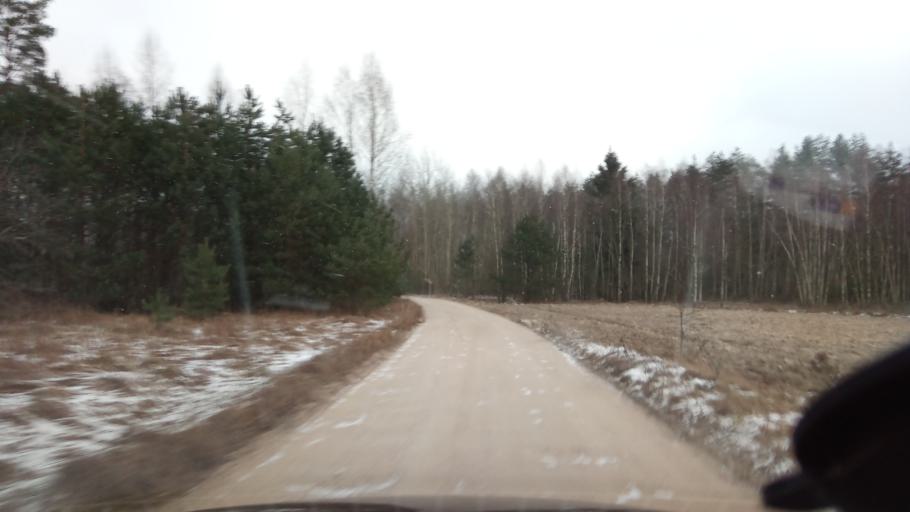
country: LT
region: Alytaus apskritis
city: Varena
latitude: 54.1223
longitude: 24.7049
